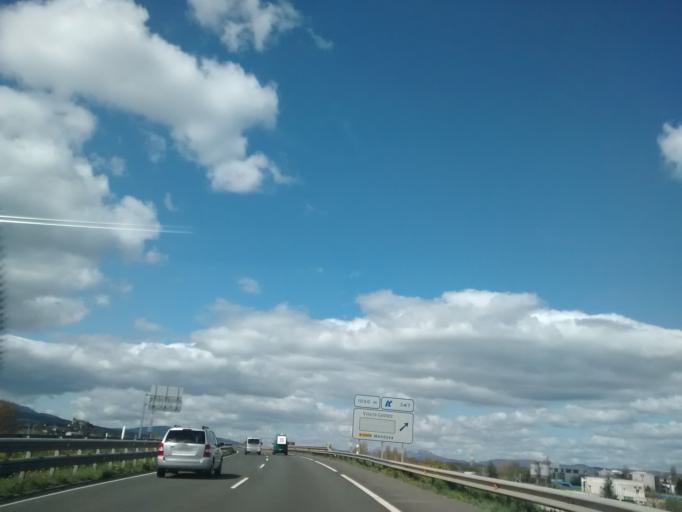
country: ES
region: Basque Country
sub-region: Provincia de Alava
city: Gasteiz / Vitoria
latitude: 42.8498
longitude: -2.7477
